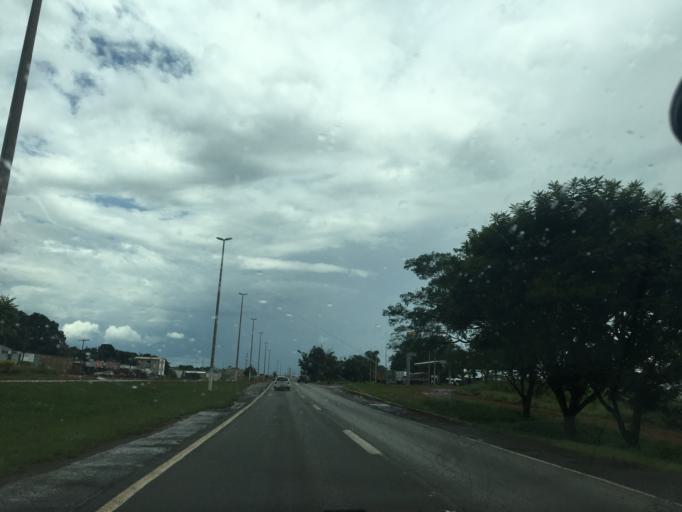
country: BR
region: Goias
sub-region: Luziania
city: Luziania
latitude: -16.2201
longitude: -47.9153
